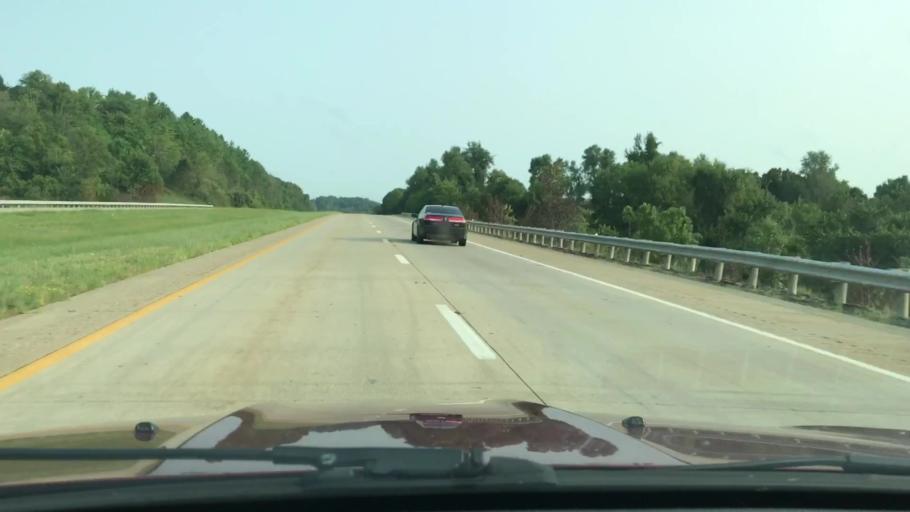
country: US
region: Ohio
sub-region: Noble County
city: Caldwell
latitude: 39.7656
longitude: -81.5440
